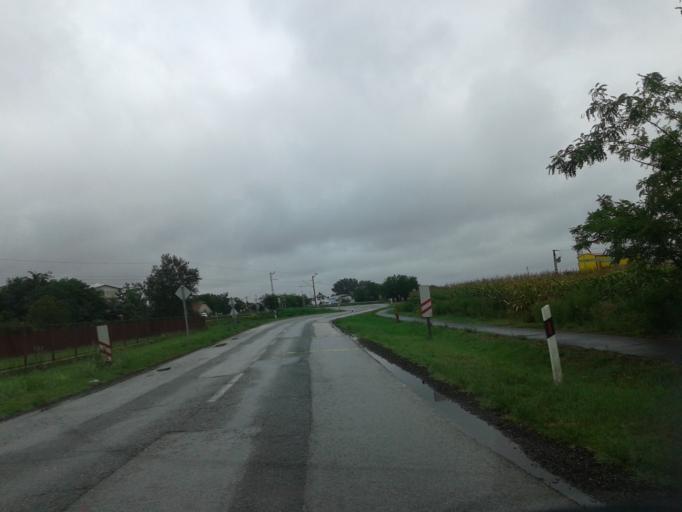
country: HU
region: Bacs-Kiskun
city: Soltvadkert
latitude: 46.5839
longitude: 19.3670
